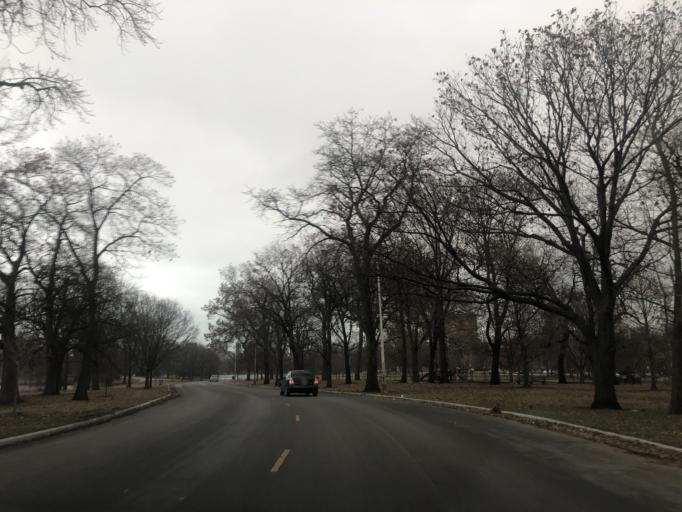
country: US
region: Illinois
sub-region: Cook County
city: Chicago
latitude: 41.7865
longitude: -87.6137
